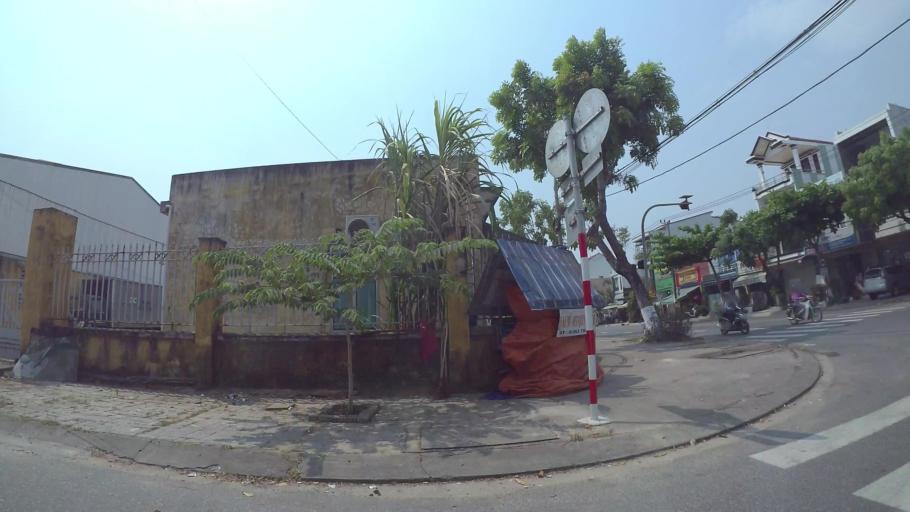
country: VN
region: Da Nang
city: Cam Le
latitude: 16.0040
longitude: 108.2074
